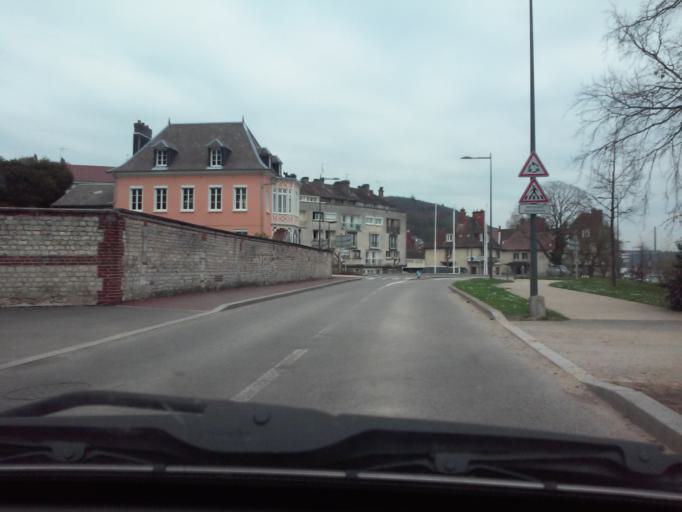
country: FR
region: Haute-Normandie
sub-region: Departement de la Seine-Maritime
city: Caudebec-en-Caux
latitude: 49.5248
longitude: 0.7221
